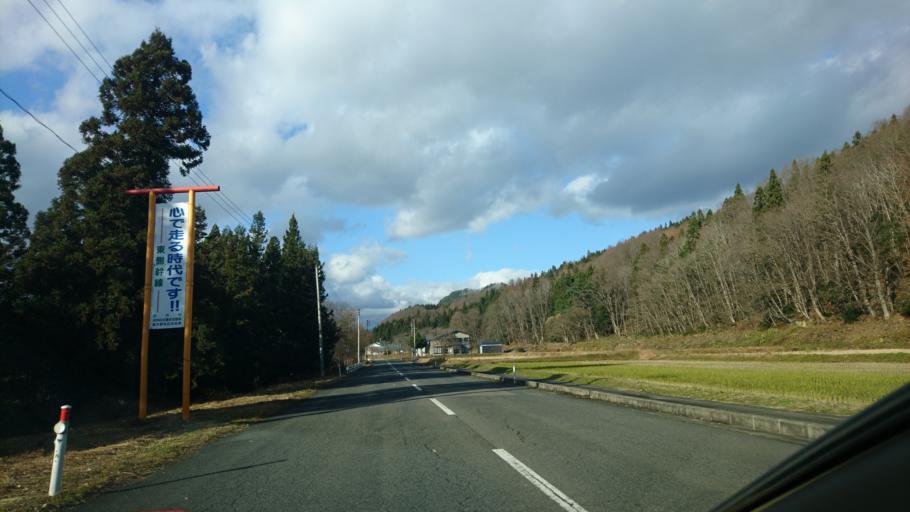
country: JP
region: Akita
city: Yokotemachi
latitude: 39.3702
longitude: 140.7704
